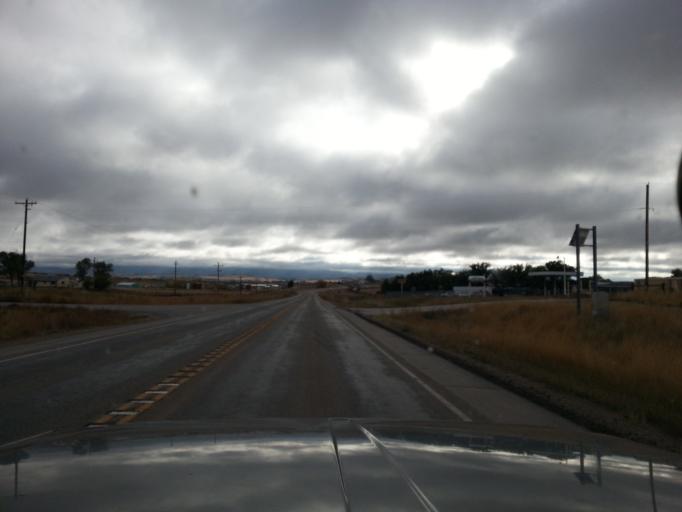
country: US
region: Wyoming
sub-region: Converse County
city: Douglas
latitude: 42.7861
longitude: -105.3680
